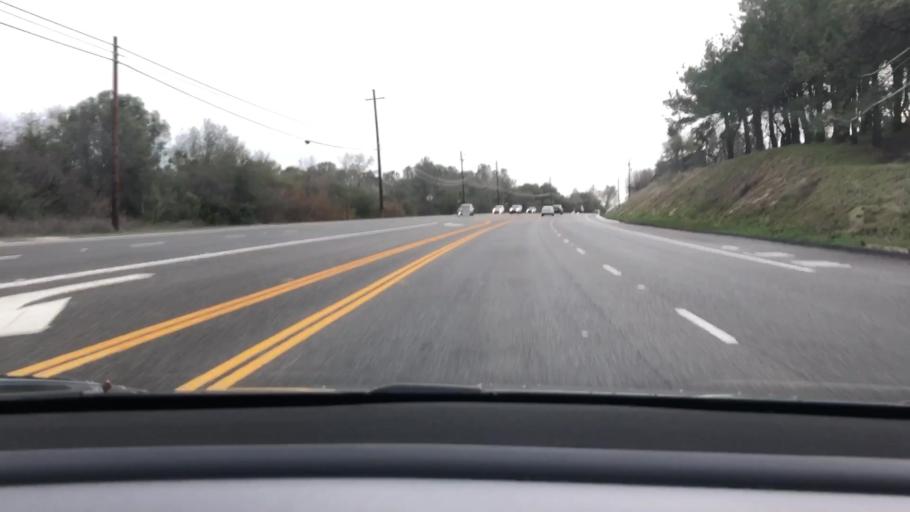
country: US
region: California
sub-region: Placer County
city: Granite Bay
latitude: 38.7237
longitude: -121.1752
